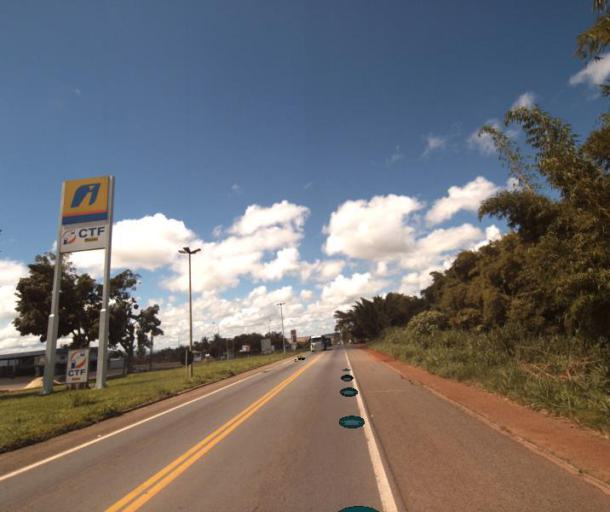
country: BR
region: Goias
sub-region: Jaragua
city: Jaragua
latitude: -15.8585
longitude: -49.2626
